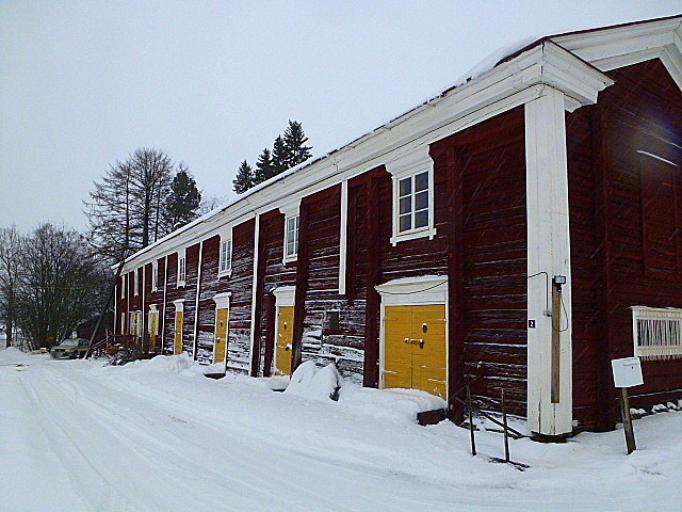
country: FI
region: Lapland
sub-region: Rovaniemi
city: Rovaniemi
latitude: 66.4824
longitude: 25.7462
